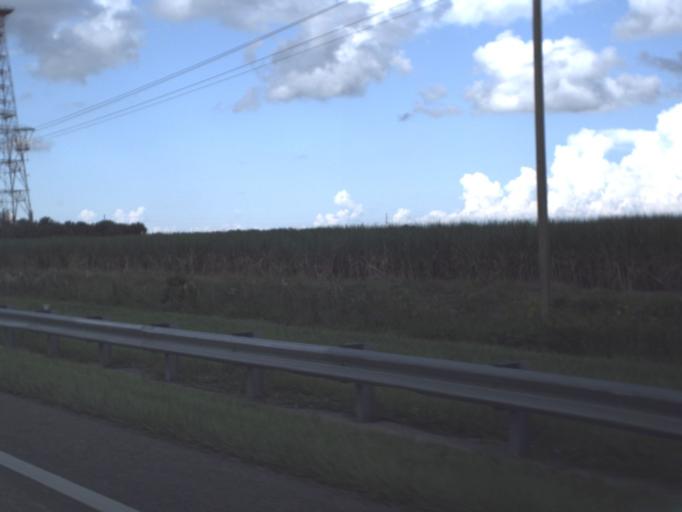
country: US
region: Florida
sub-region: Glades County
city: Moore Haven
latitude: 26.7644
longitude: -81.0829
